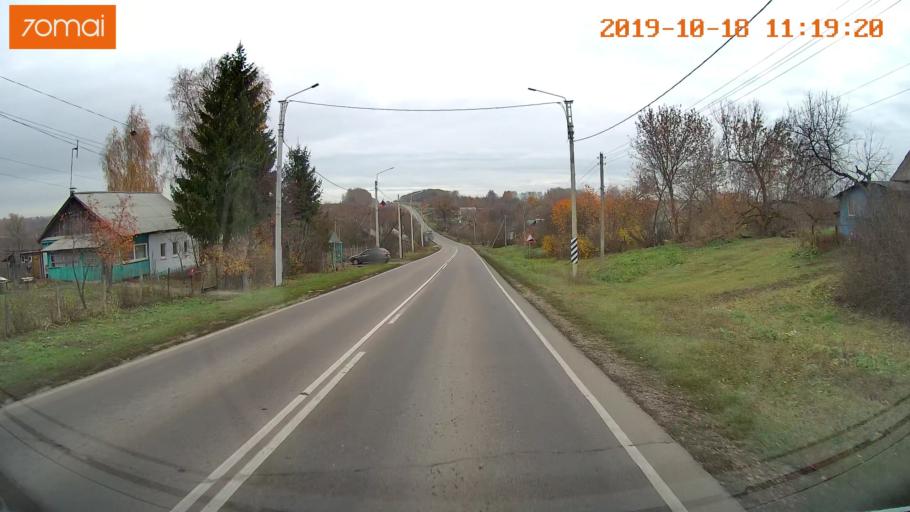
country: RU
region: Tula
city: Kimovsk
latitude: 54.0455
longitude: 38.5533
